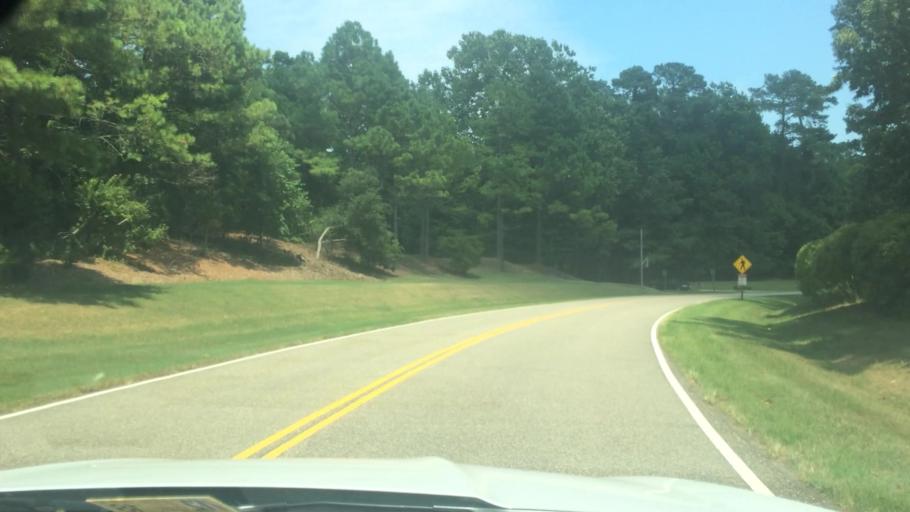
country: US
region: Virginia
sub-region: City of Williamsburg
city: Williamsburg
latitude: 37.2246
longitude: -76.6484
